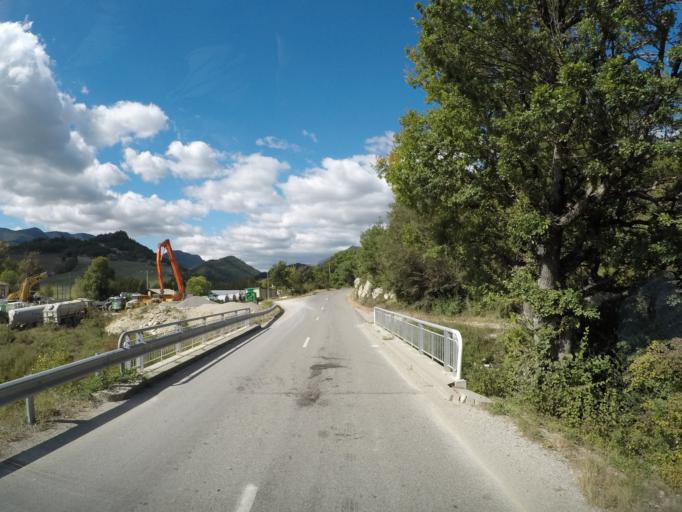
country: FR
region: Provence-Alpes-Cote d'Azur
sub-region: Departement des Hautes-Alpes
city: Laragne-Monteglin
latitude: 44.1673
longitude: 5.7645
